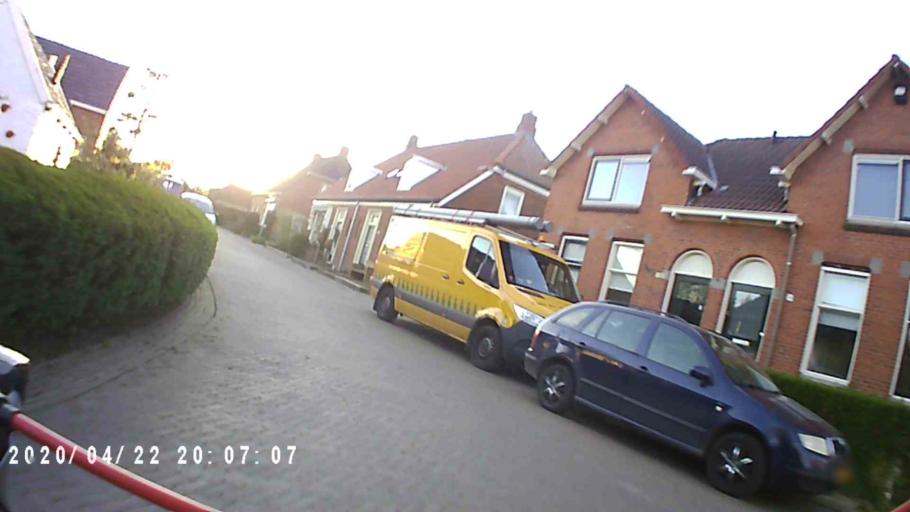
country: NL
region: Groningen
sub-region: Gemeente Zuidhorn
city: Aduard
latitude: 53.3069
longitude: 6.4673
